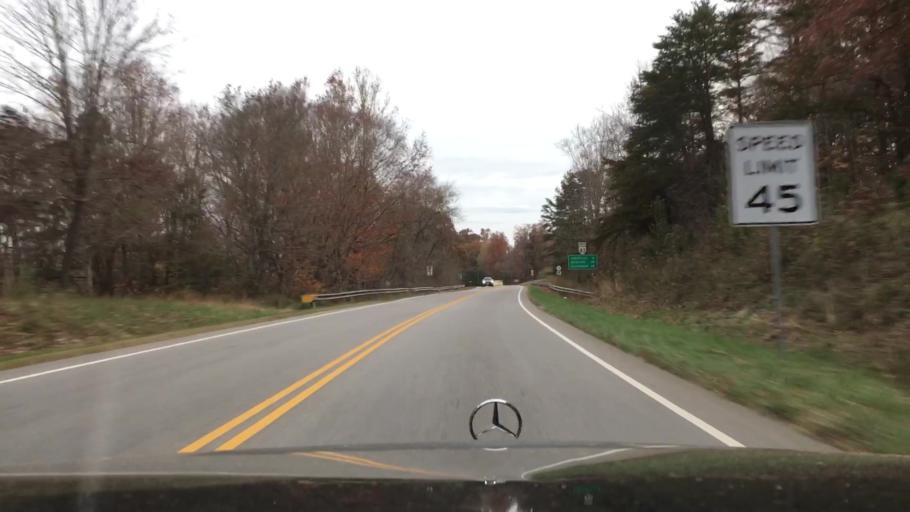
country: US
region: Virginia
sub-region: Campbell County
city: Altavista
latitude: 37.1305
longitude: -79.3072
